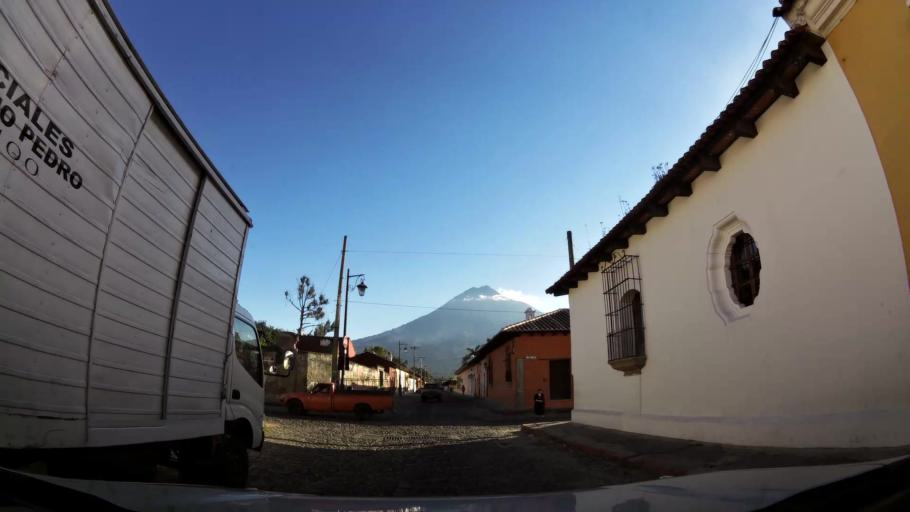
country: GT
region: Sacatepequez
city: Antigua Guatemala
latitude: 14.5545
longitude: -90.7332
